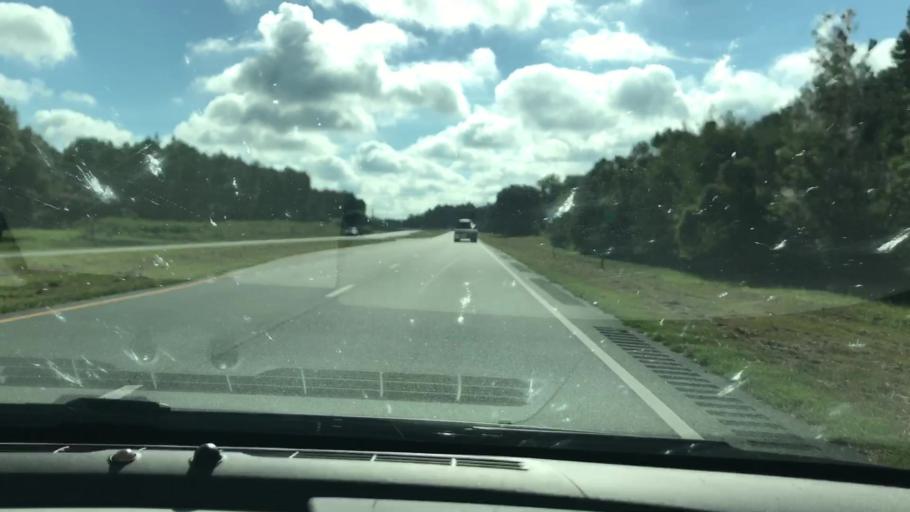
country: US
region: Georgia
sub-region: Worth County
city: Sylvester
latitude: 31.5513
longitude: -83.9728
